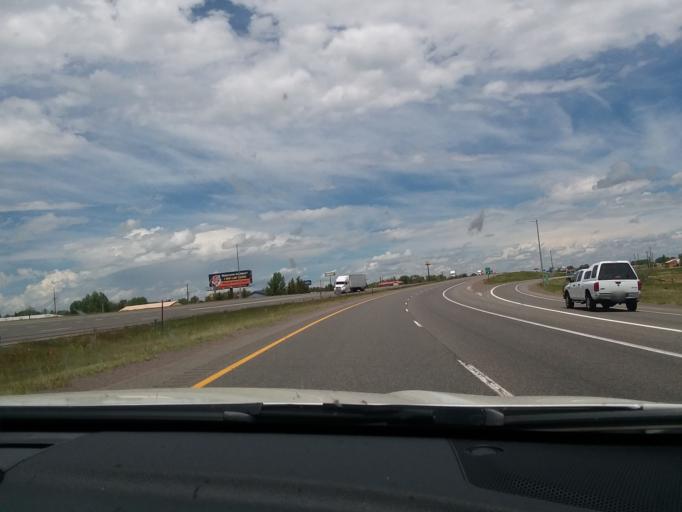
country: US
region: Wyoming
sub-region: Albany County
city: Laramie
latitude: 41.3046
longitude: -105.6135
